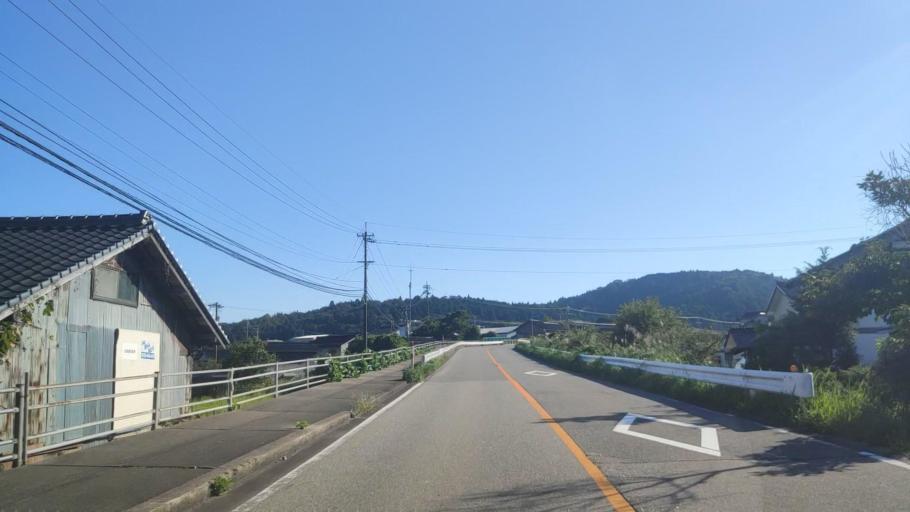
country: JP
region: Ishikawa
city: Nanao
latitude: 37.1446
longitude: 136.8721
